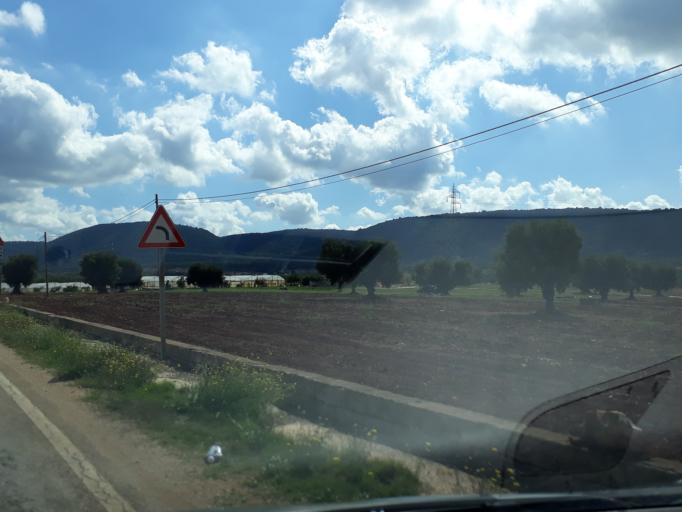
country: IT
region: Apulia
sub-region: Provincia di Brindisi
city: Pezze di Greco
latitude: 40.8041
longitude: 17.3940
